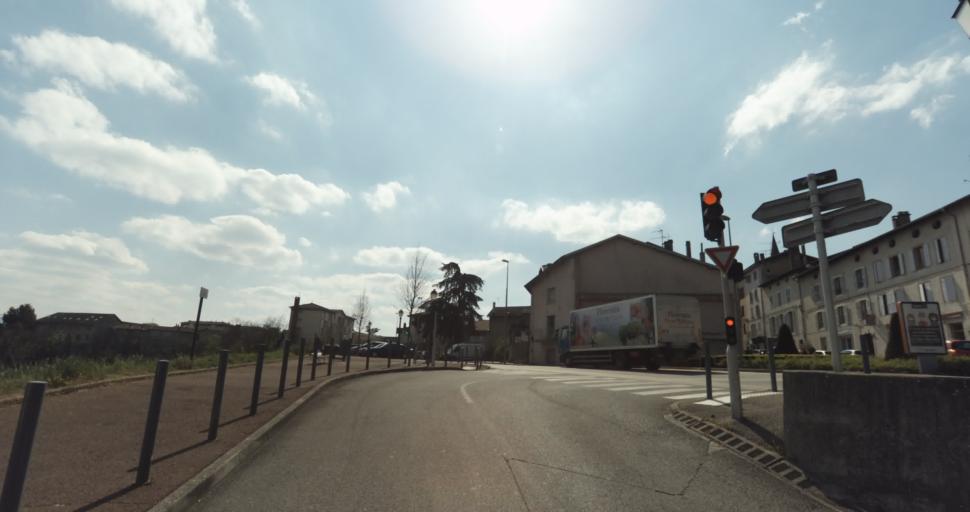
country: FR
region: Rhone-Alpes
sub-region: Departement de l'Isere
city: Saint-Marcellin
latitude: 45.1550
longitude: 5.3243
